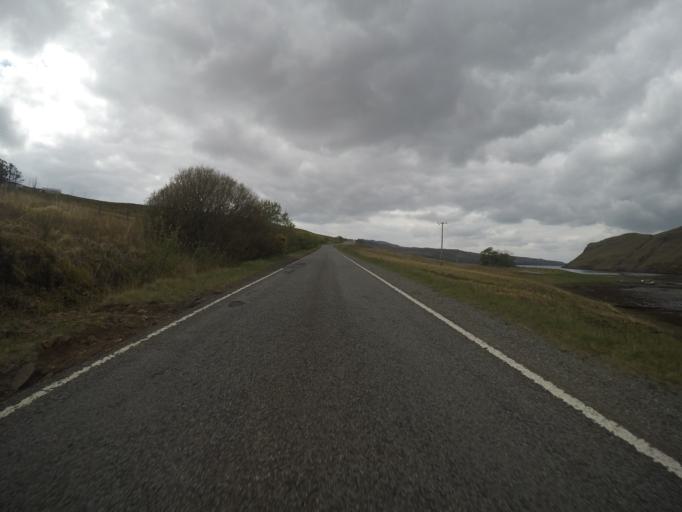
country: GB
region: Scotland
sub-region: Highland
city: Isle of Skye
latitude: 57.2962
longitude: -6.3205
